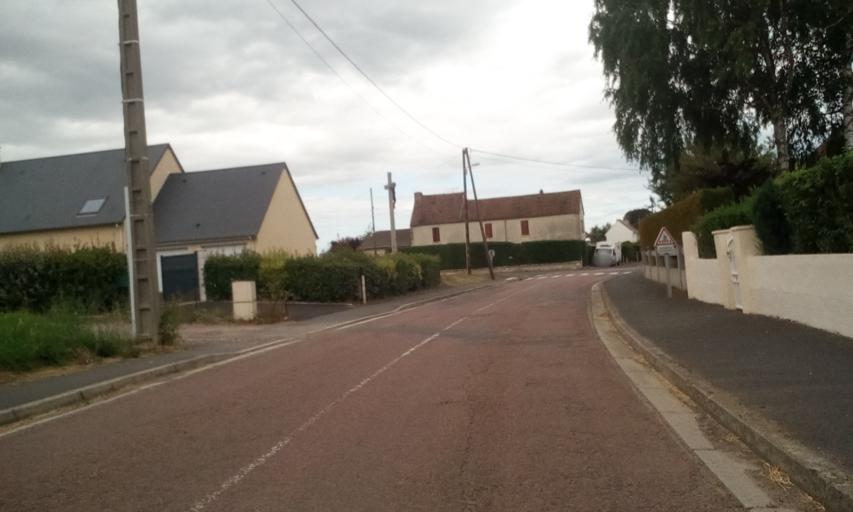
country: FR
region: Lower Normandy
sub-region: Departement du Calvados
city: Sannerville
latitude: 49.1515
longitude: -0.2253
